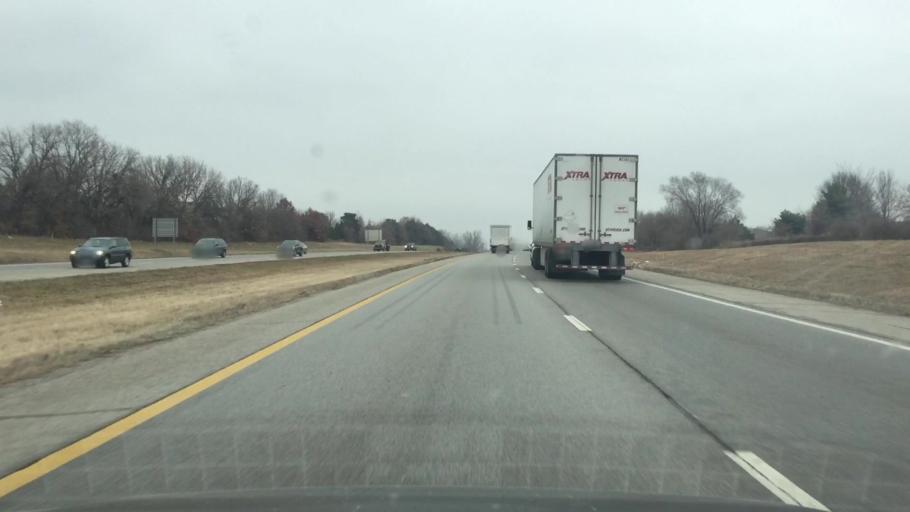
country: US
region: Kansas
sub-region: Johnson County
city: Lenexa
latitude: 38.8620
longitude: -94.6775
